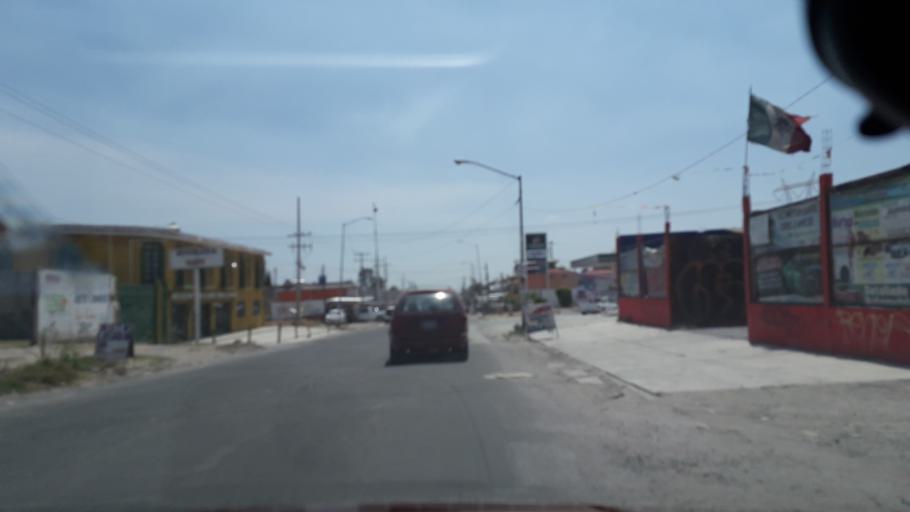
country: MX
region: Puebla
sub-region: Puebla
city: Primero de Mayo
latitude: 19.0744
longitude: -98.1137
